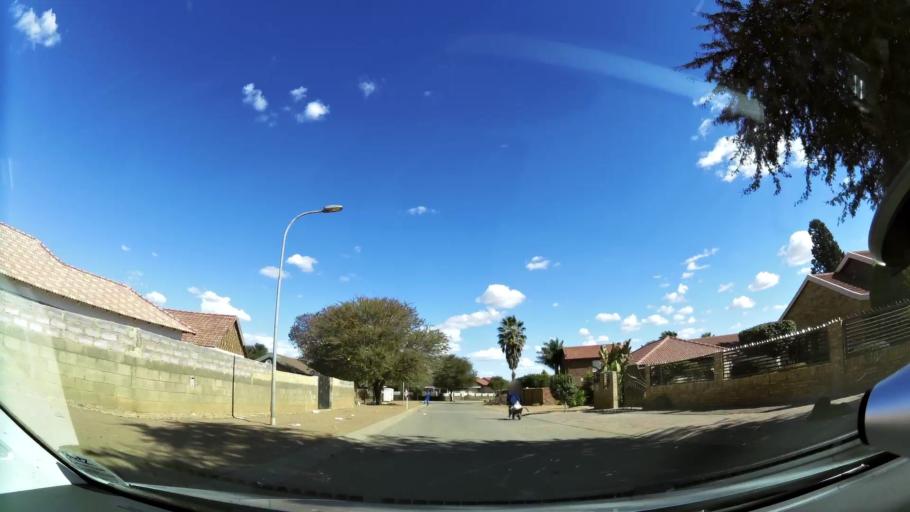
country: ZA
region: North-West
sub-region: Dr Kenneth Kaunda District Municipality
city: Klerksdorp
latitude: -26.8746
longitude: 26.5862
